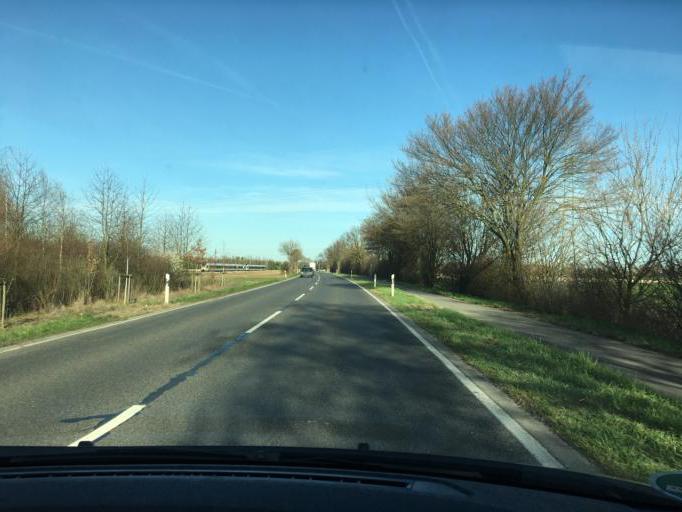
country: DE
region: North Rhine-Westphalia
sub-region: Regierungsbezirk Dusseldorf
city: Kaarst
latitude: 51.1974
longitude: 6.6311
